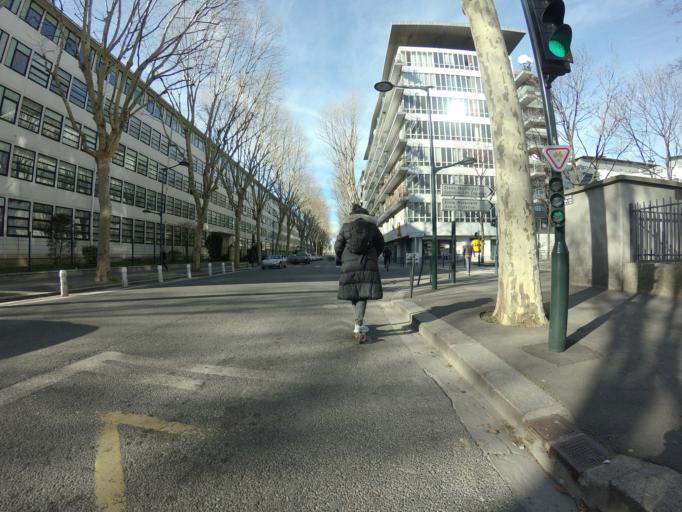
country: FR
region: Ile-de-France
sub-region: Departement des Hauts-de-Seine
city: Clichy
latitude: 48.9090
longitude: 2.3073
